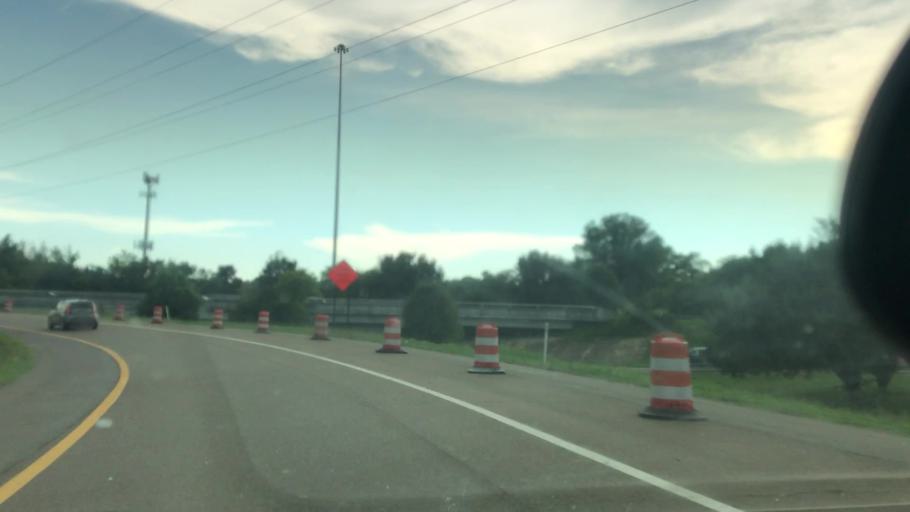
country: US
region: Tennessee
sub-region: Shelby County
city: Germantown
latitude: 35.1034
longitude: -89.8710
